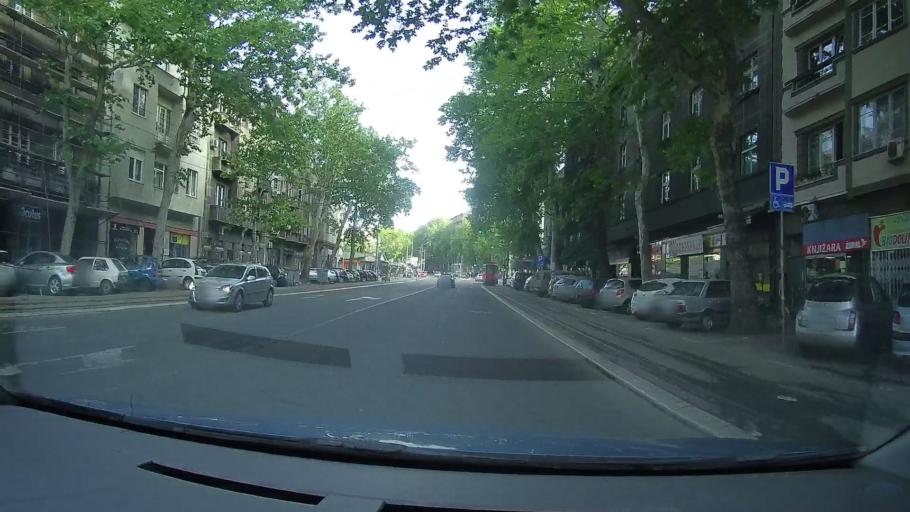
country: RS
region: Central Serbia
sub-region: Belgrade
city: Stari Grad
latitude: 44.8196
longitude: 20.4661
